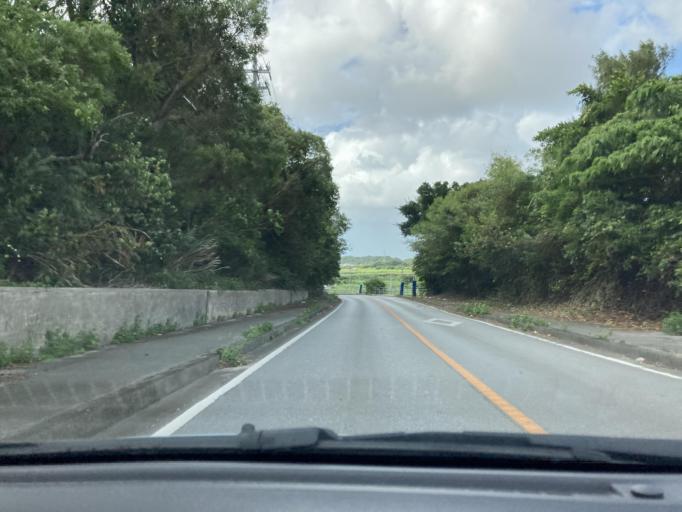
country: JP
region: Okinawa
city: Itoman
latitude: 26.1102
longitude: 127.6938
